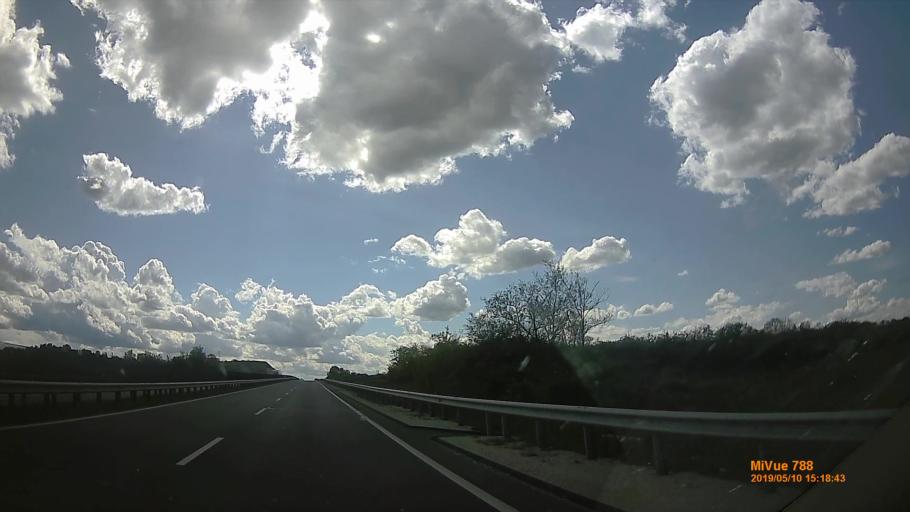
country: HU
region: Veszprem
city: Hajmasker
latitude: 47.1416
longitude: 18.0402
